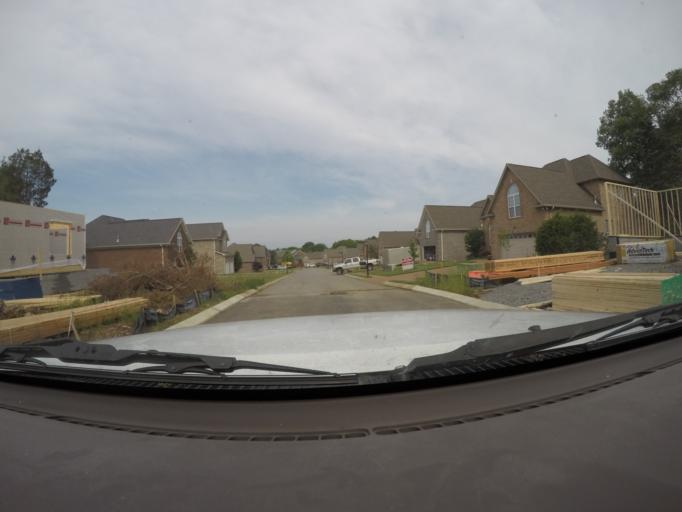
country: US
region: Tennessee
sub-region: Wilson County
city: Mount Juliet
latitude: 36.2205
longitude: -86.4868
